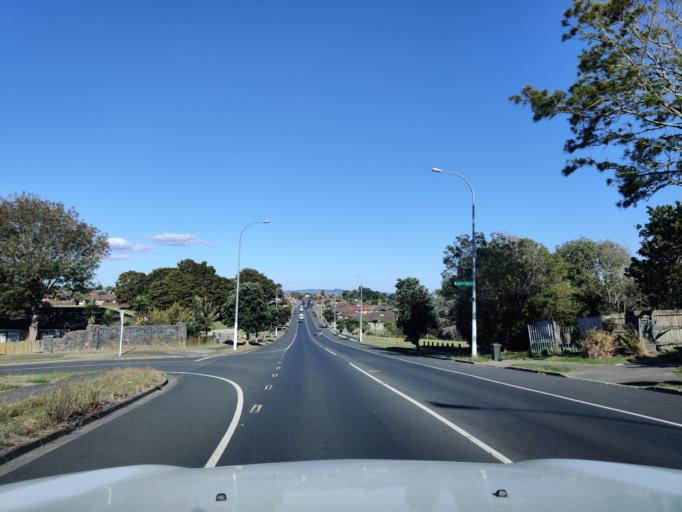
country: NZ
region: Auckland
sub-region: Auckland
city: Takanini
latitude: -37.0366
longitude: 174.8724
